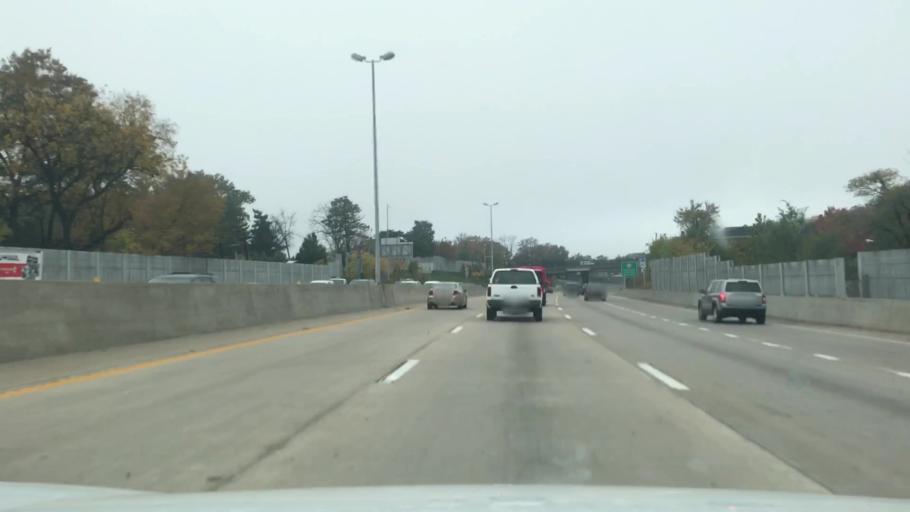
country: US
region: Missouri
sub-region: Saint Louis County
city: Richmond Heights
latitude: 38.6291
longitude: -90.3093
